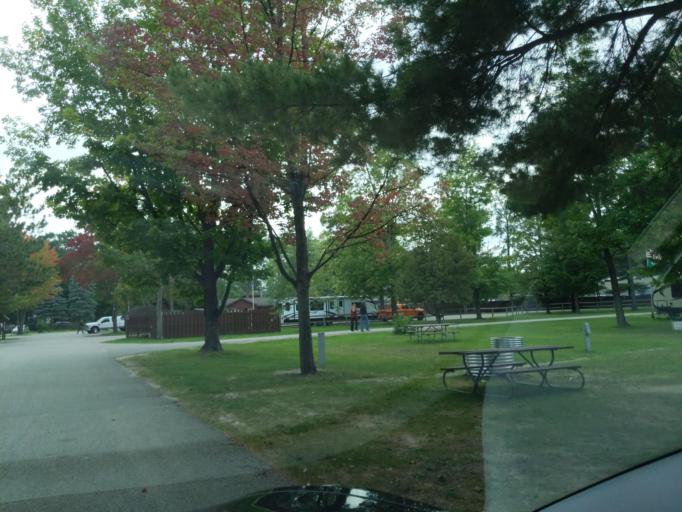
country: US
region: Michigan
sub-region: Wexford County
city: Cadillac
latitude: 44.2378
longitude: -85.4522
